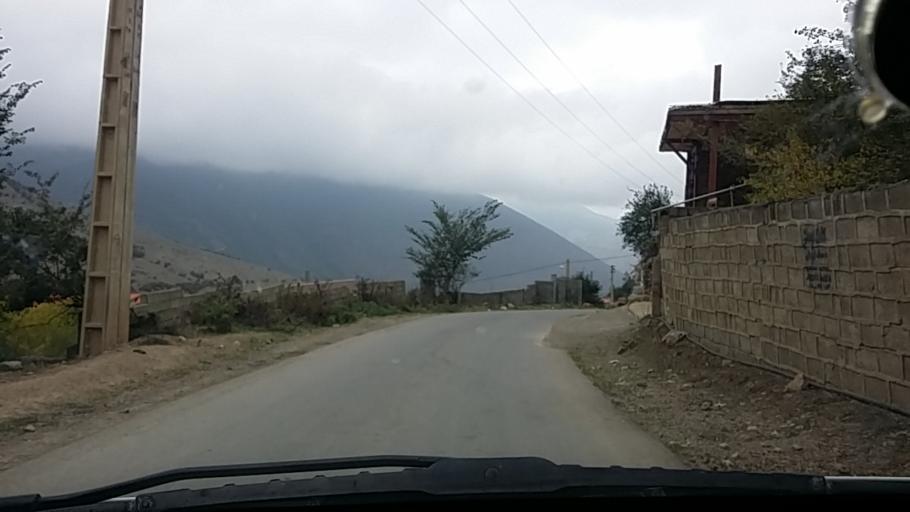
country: IR
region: Mazandaran
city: `Abbasabad
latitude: 36.4728
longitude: 51.1401
